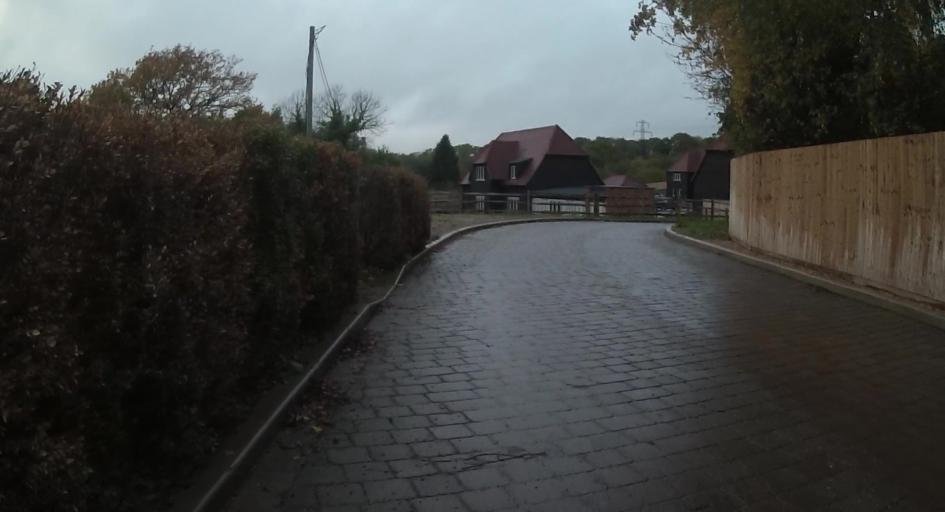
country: GB
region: England
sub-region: Surrey
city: Farnham
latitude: 51.2243
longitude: -0.8103
